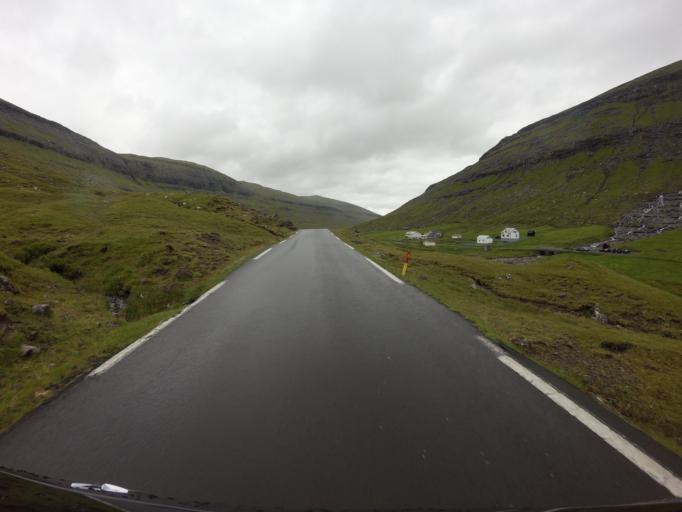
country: FO
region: Streymoy
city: Vestmanna
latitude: 62.2441
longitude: -7.1701
